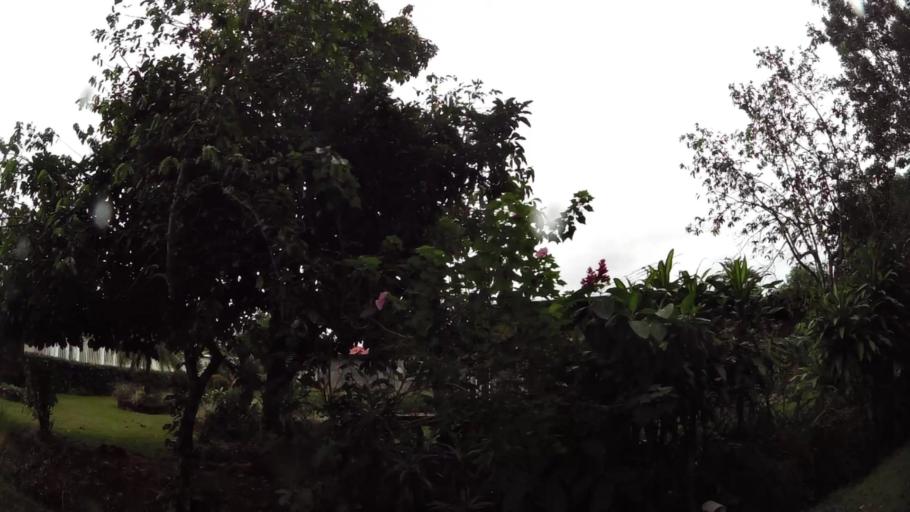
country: PA
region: Chiriqui
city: David
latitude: 8.3997
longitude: -82.4568
